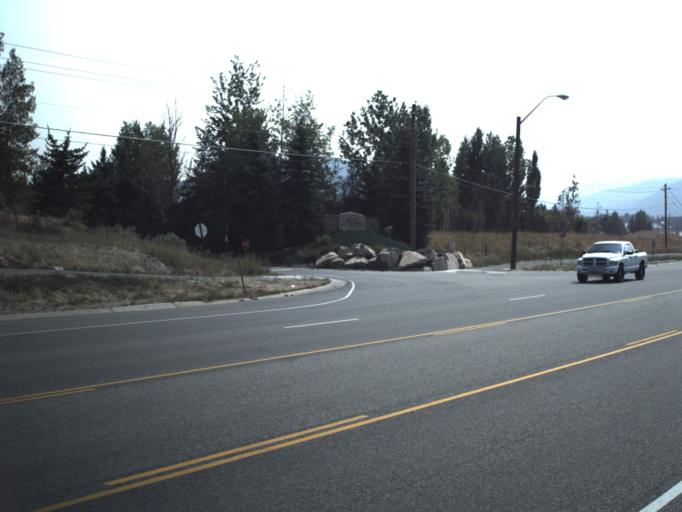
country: US
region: Utah
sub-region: Summit County
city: Snyderville
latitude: 40.7060
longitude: -111.5468
